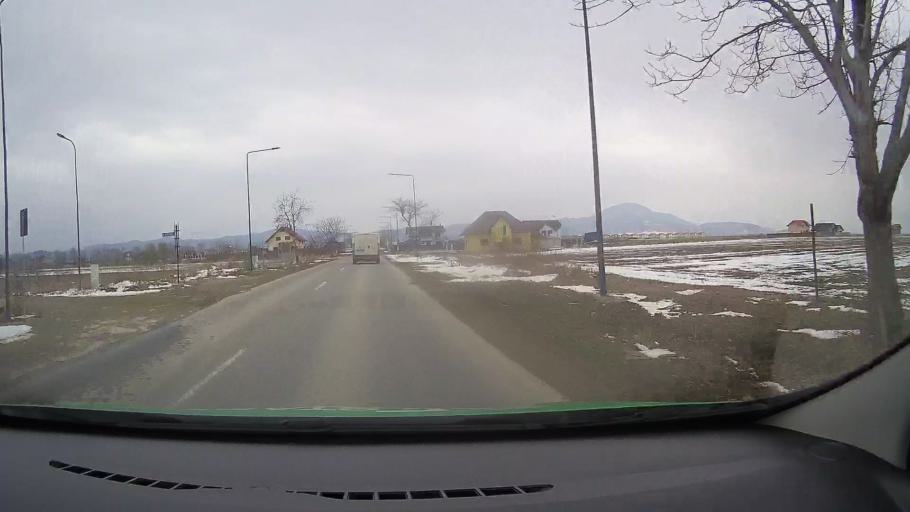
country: RO
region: Brasov
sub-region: Comuna Cristian
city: Cristian
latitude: 45.6269
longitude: 25.4720
